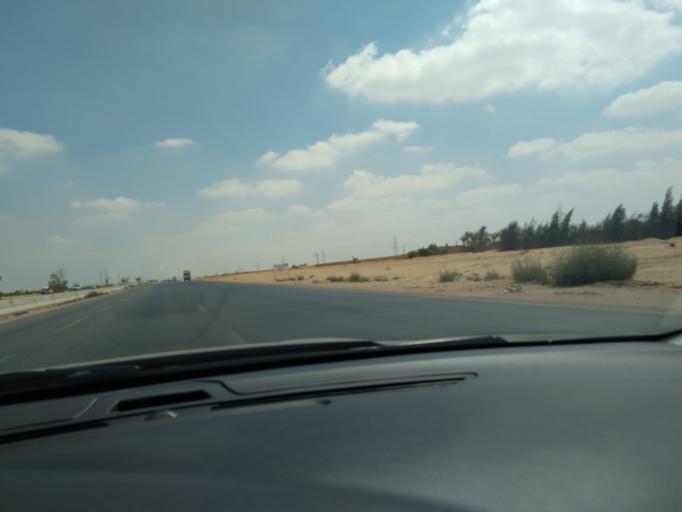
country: EG
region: Al Isma'iliyah
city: At Tall al Kabir
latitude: 30.3453
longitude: 31.8743
